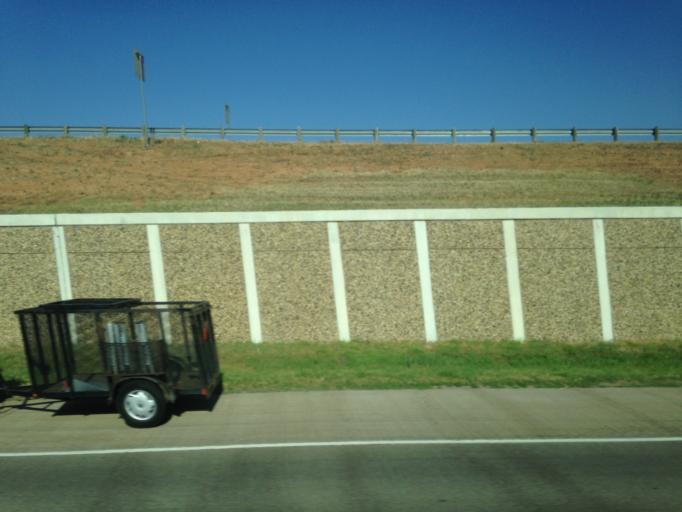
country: US
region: Texas
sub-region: Lubbock County
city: Lubbock
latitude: 33.5521
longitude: -101.8452
